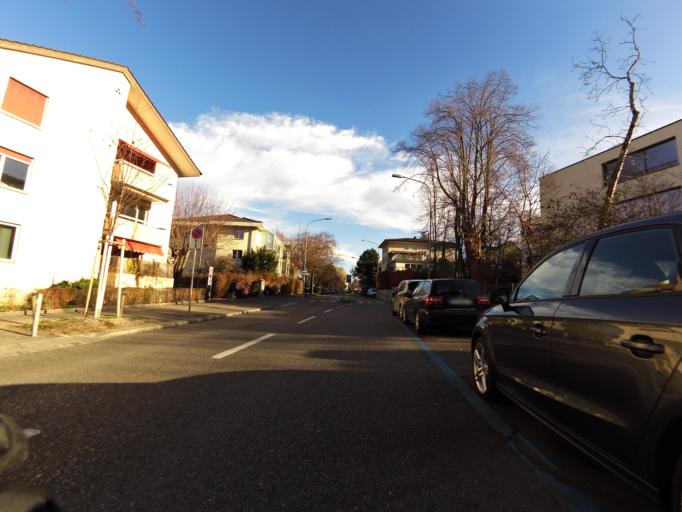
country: CH
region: Zurich
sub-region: Bezirk Zuerich
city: Zuerich (Kreis 9) / Albisrieden
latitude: 47.3732
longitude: 8.4849
